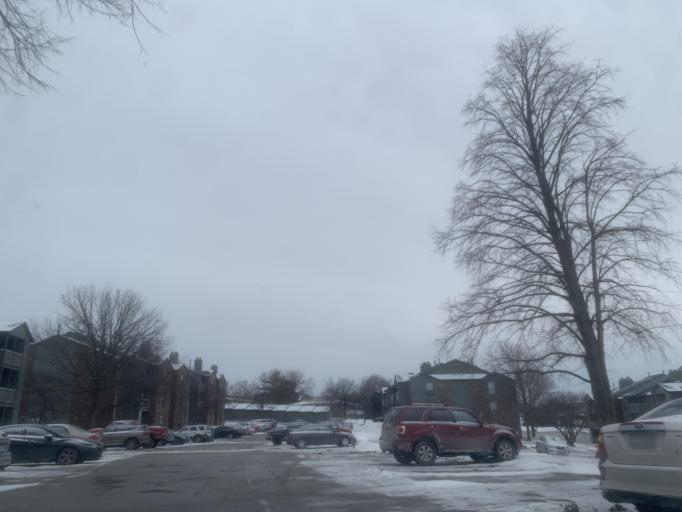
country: US
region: Nebraska
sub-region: Douglas County
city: Ralston
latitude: 41.2717
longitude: -96.0835
